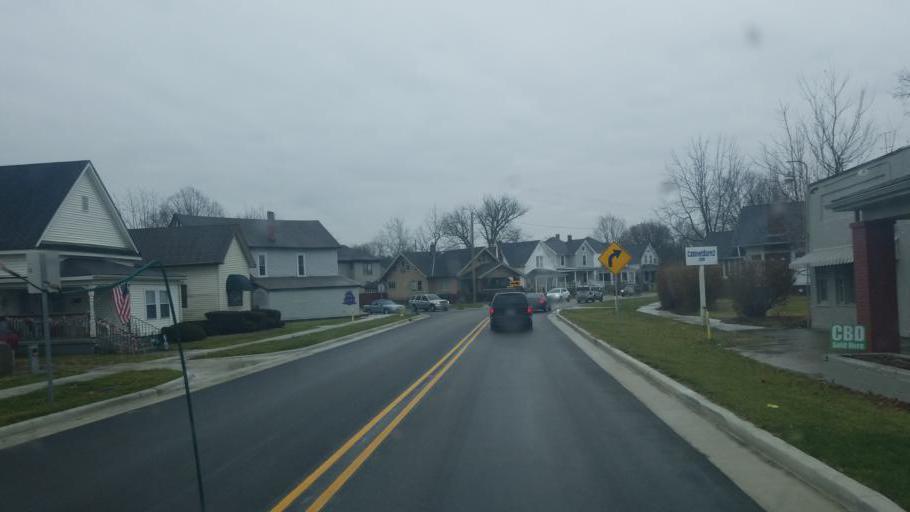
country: US
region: Indiana
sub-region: Shelby County
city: Shelbyville
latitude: 39.5161
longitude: -85.7757
